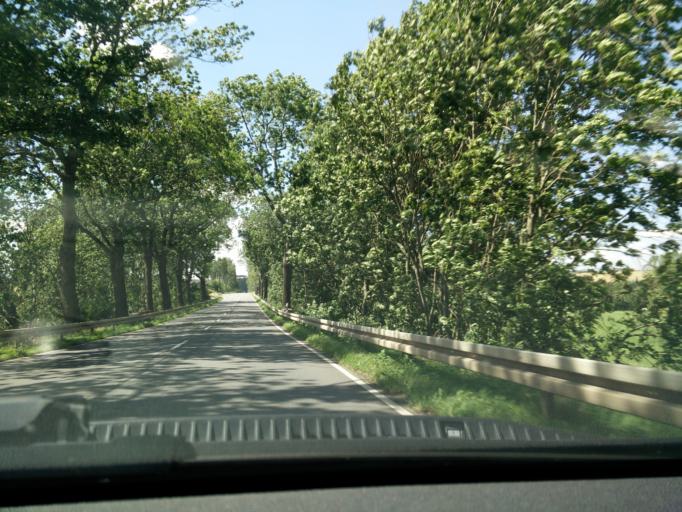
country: DE
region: Saxony
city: Penig
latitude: 50.9264
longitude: 12.7029
